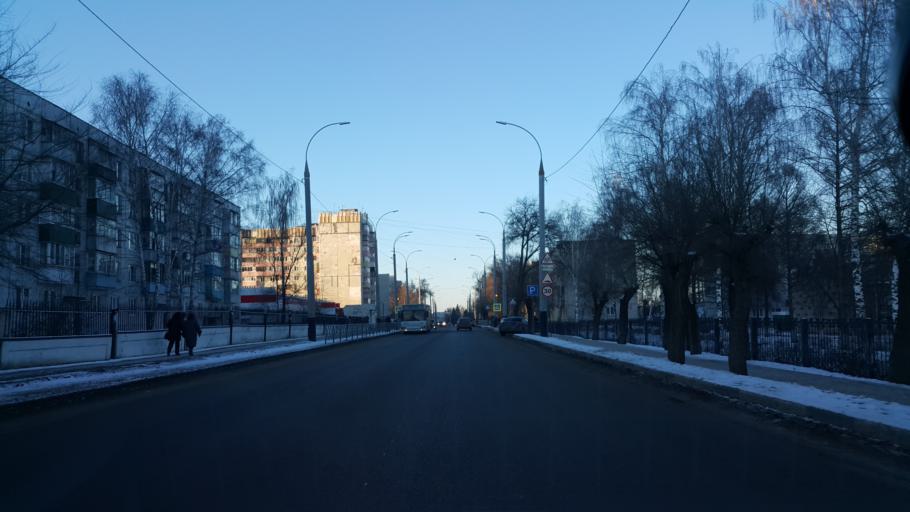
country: RU
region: Tambov
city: Pokrovo-Prigorodnoye
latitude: 52.7061
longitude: 41.3986
